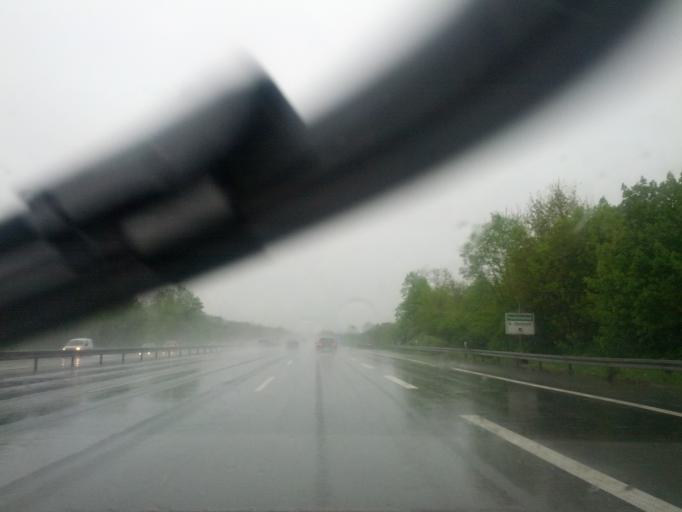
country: DE
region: North Rhine-Westphalia
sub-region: Regierungsbezirk Koln
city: Merheim
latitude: 50.9520
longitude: 7.0524
